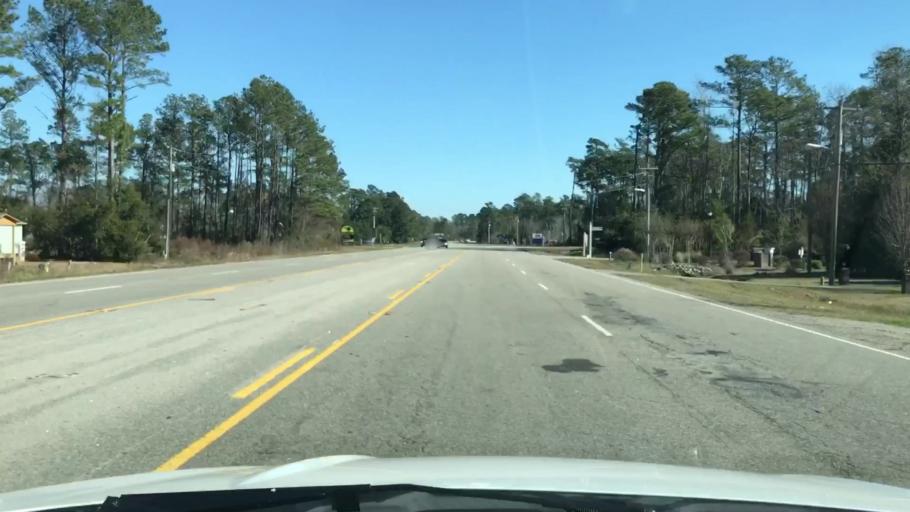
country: US
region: South Carolina
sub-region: Horry County
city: Garden City
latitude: 33.6299
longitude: -79.0264
